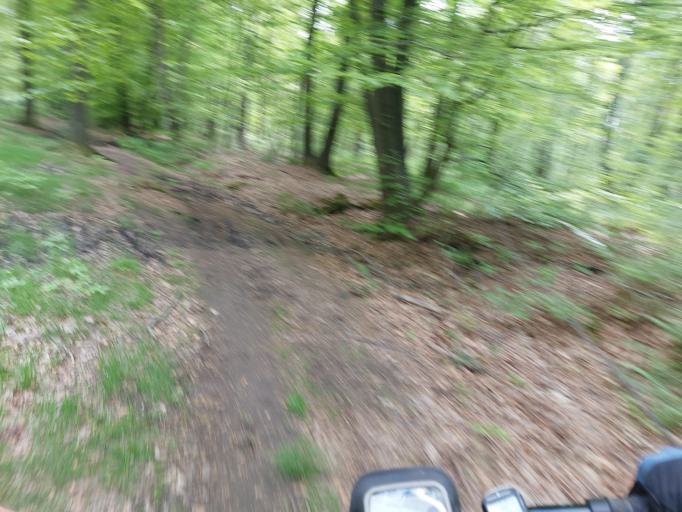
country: BE
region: Wallonia
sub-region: Province du Hainaut
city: Jurbise
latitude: 50.5026
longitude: 3.8535
